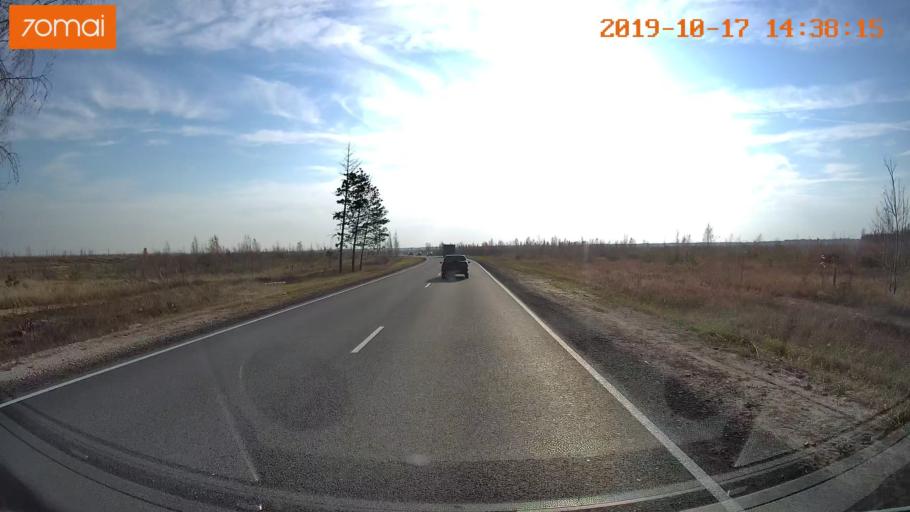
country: RU
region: Rjazan
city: Solotcha
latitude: 54.8722
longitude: 39.9858
